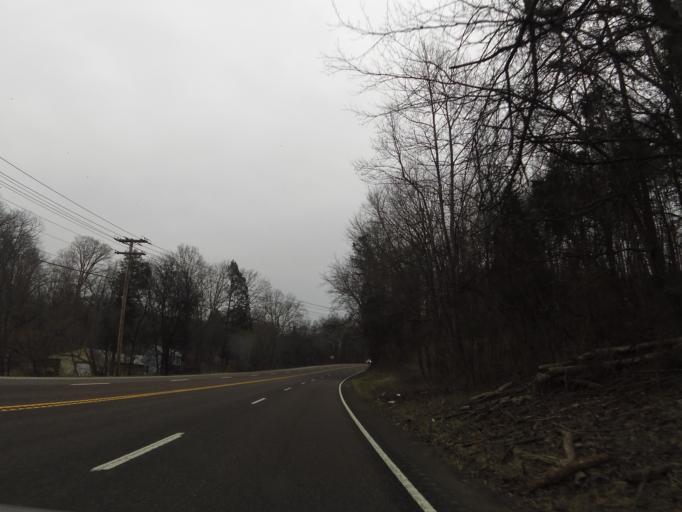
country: US
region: Tennessee
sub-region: Anderson County
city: Clinton
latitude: 36.0604
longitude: -84.1225
